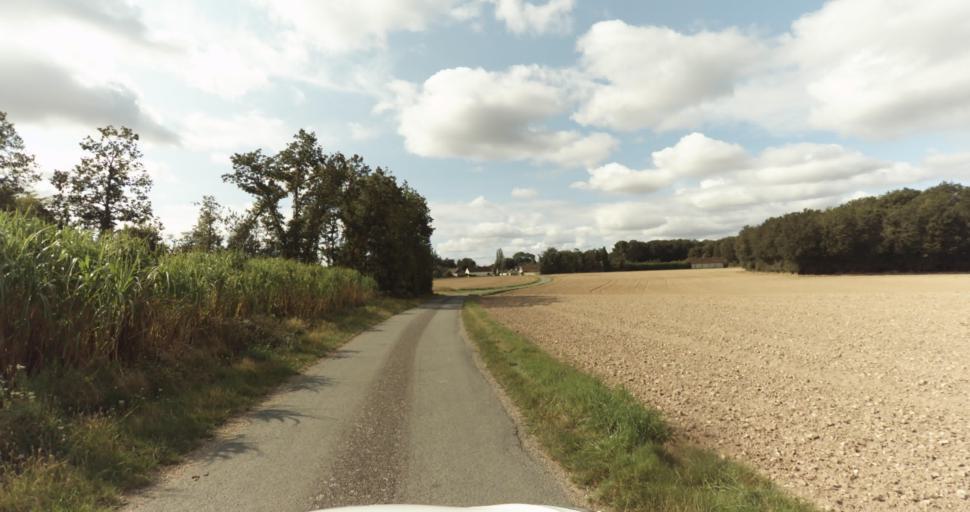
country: FR
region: Haute-Normandie
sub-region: Departement de l'Eure
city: Tillieres-sur-Avre
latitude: 48.7619
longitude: 1.1102
